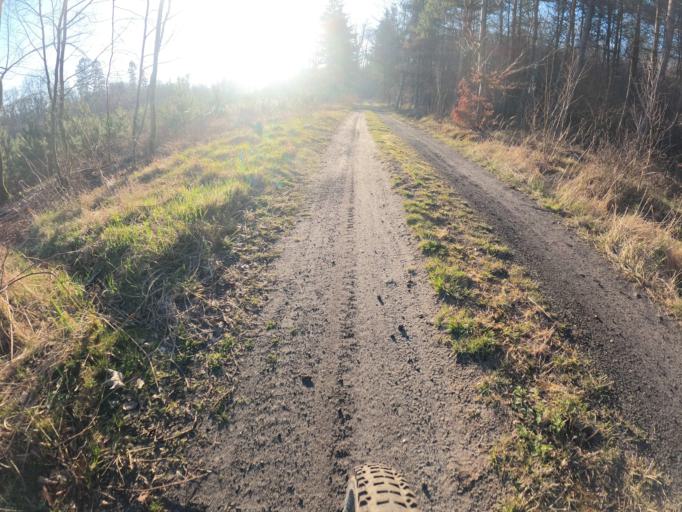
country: PL
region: West Pomeranian Voivodeship
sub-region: Powiat gryficki
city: Brojce
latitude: 53.9599
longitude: 15.3765
